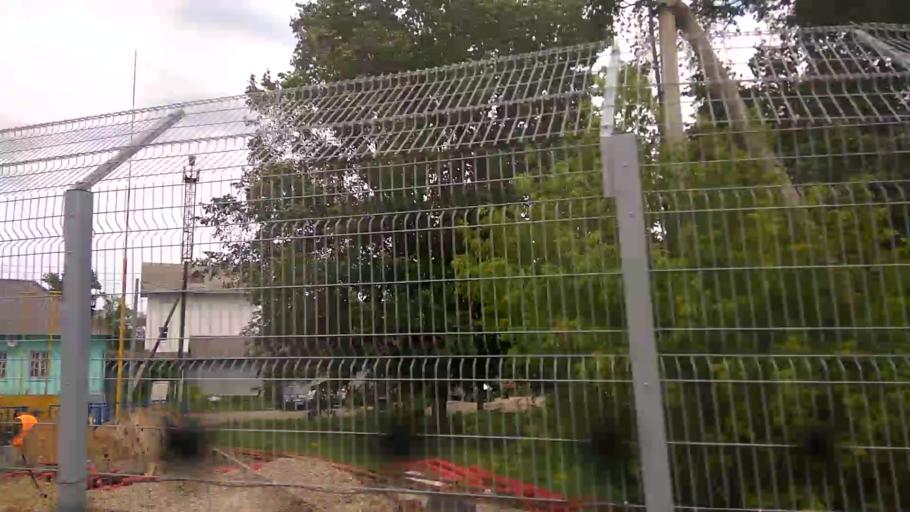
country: RU
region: Moskovskaya
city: Kolomna
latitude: 55.0849
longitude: 38.8060
